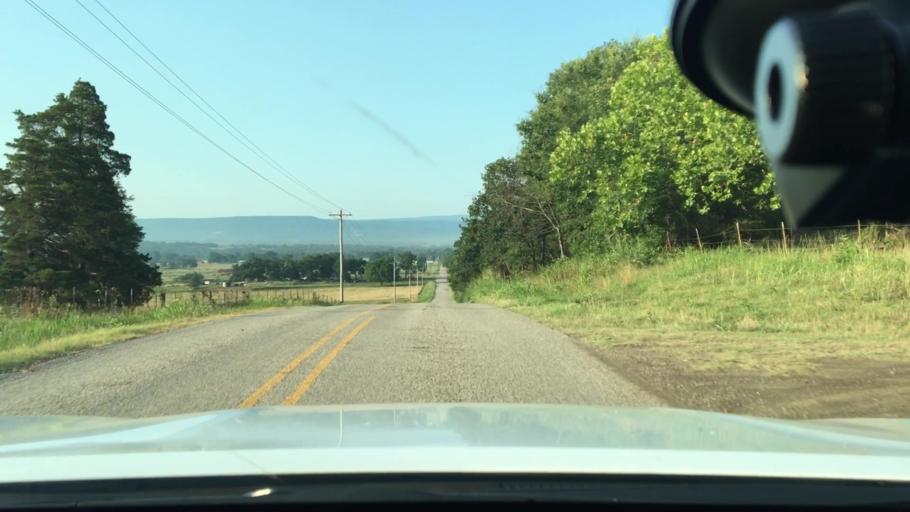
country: US
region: Arkansas
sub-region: Johnson County
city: Coal Hill
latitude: 35.3508
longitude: -93.6133
